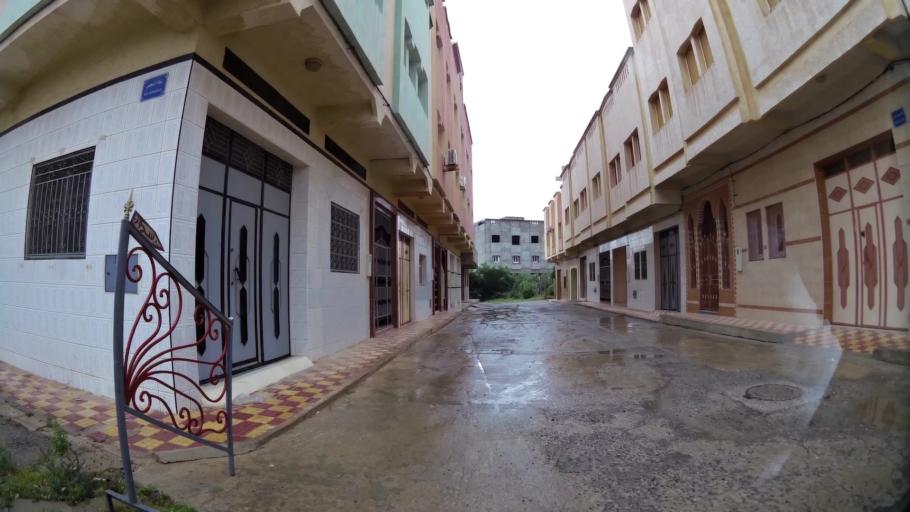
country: MA
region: Oriental
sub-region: Nador
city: Nador
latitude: 35.1549
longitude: -2.9749
